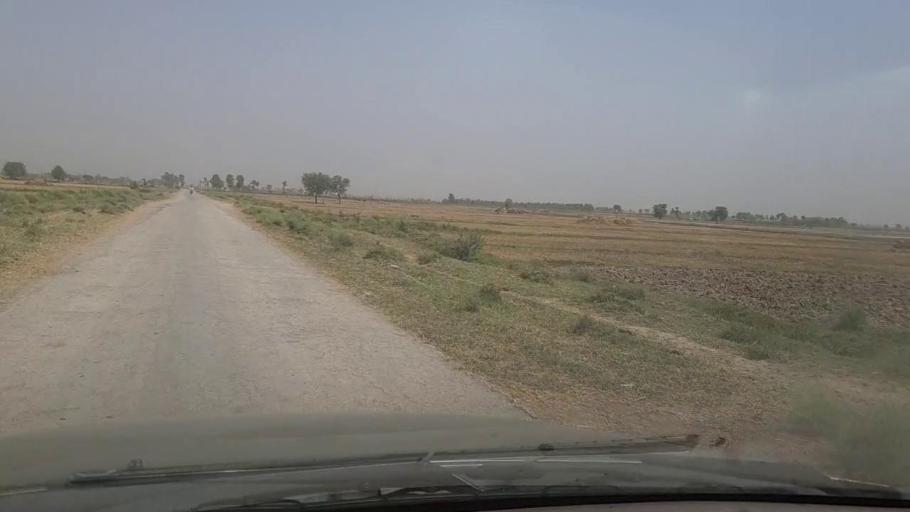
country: PK
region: Sindh
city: Madeji
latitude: 27.8129
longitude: 68.3979
